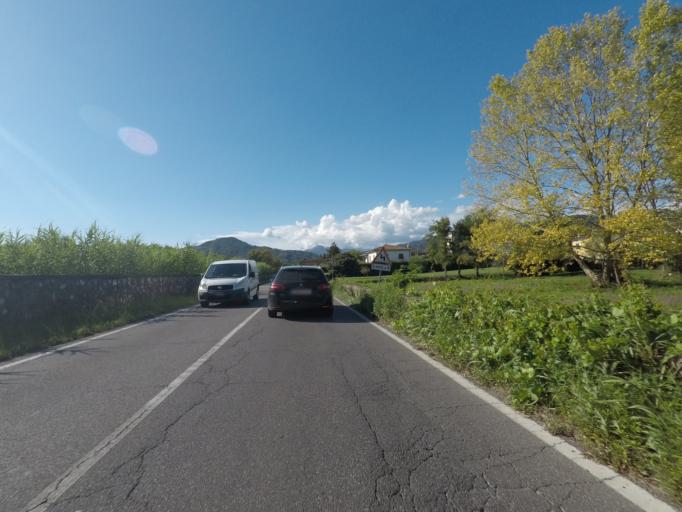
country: IT
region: Tuscany
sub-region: Provincia di Lucca
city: Lucca
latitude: 43.8741
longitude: 10.4929
